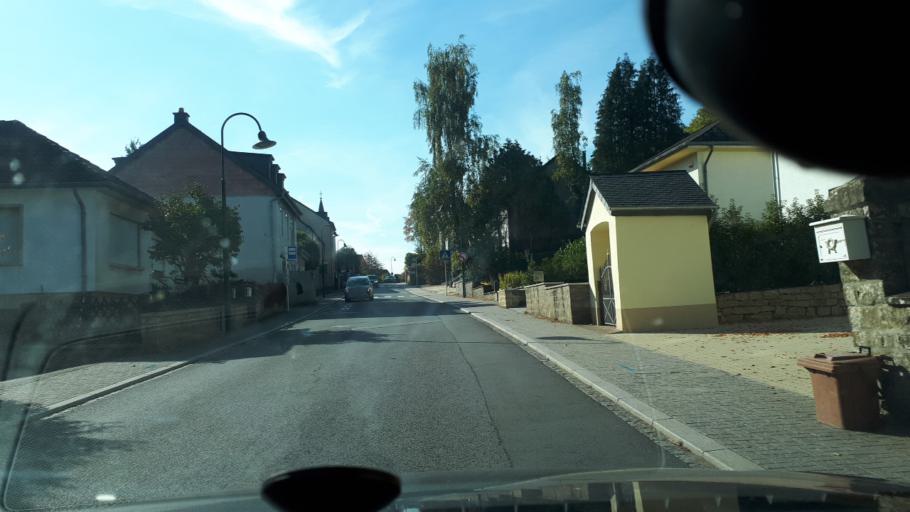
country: LU
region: Grevenmacher
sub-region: Canton de Grevenmacher
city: Flaxweiler
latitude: 49.6672
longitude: 6.3014
